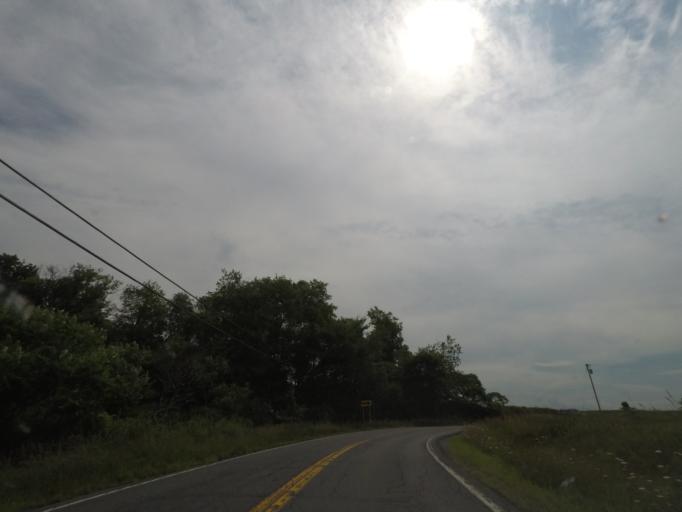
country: US
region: New York
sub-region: Rensselaer County
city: Wynantskill
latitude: 42.7368
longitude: -73.6073
